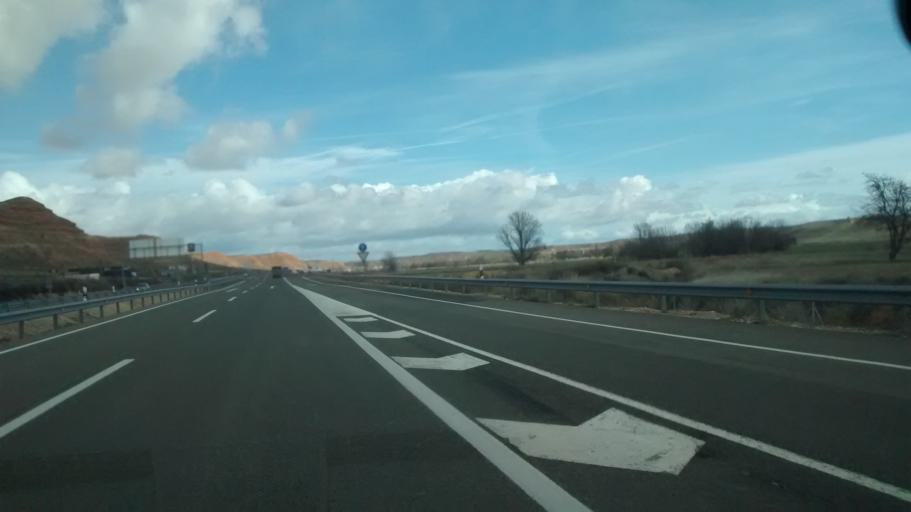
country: ES
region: Castille and Leon
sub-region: Provincia de Soria
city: Santa Maria de Huerta
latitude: 41.2452
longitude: -2.2223
